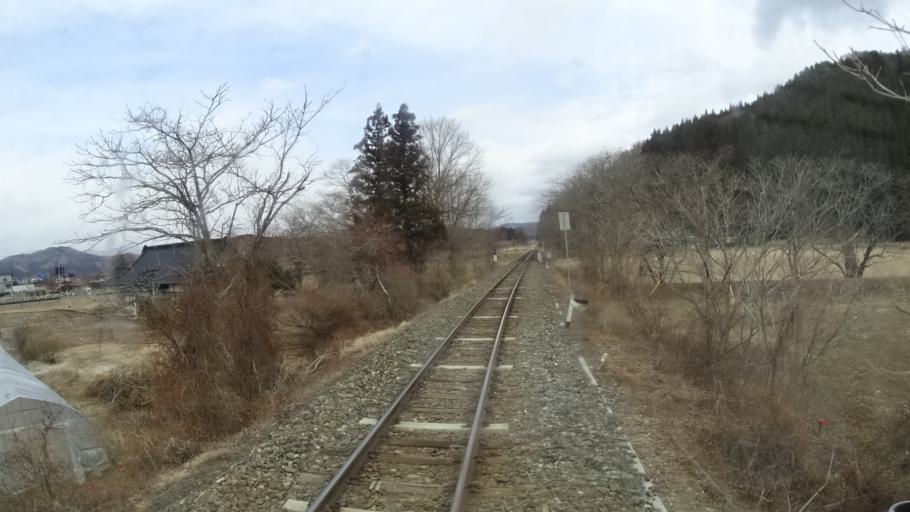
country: JP
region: Iwate
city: Tono
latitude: 39.2681
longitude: 141.5888
